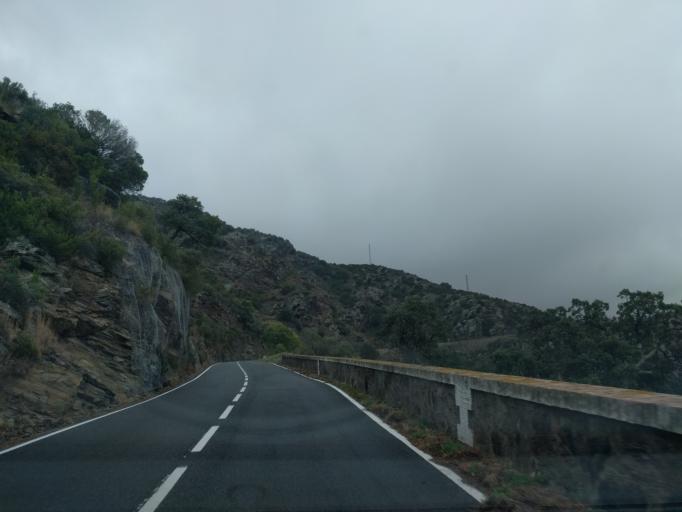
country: ES
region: Catalonia
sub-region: Provincia de Girona
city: Cadaques
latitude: 42.3042
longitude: 3.2273
